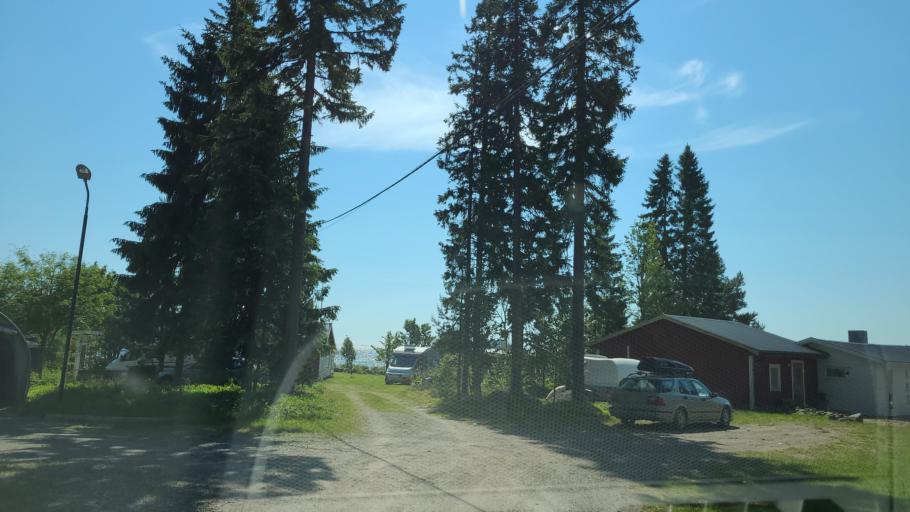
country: SE
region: Vaesterbotten
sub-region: Robertsfors Kommun
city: Robertsfors
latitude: 64.1385
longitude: 20.9633
